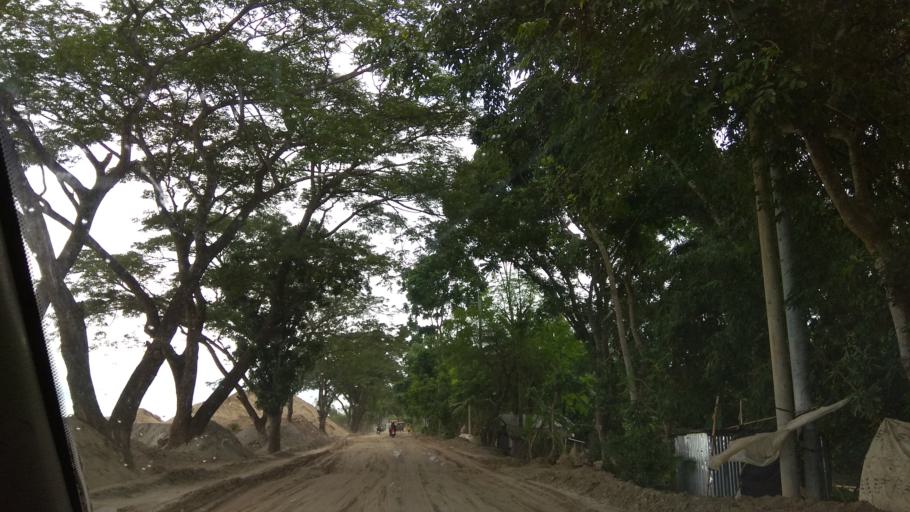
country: BD
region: Khulna
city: Kalia
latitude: 23.1994
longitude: 89.6972
